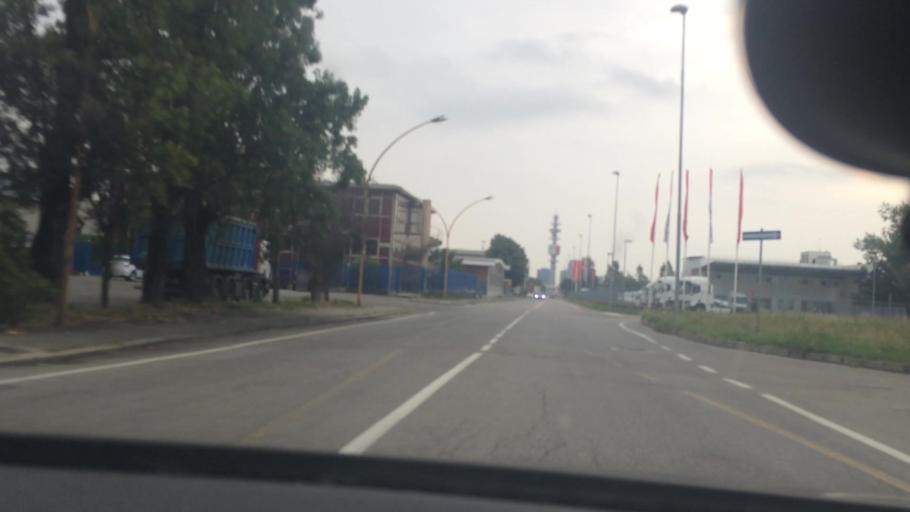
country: IT
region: Lombardy
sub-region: Citta metropolitana di Milano
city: Pero
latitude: 45.5032
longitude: 9.0800
